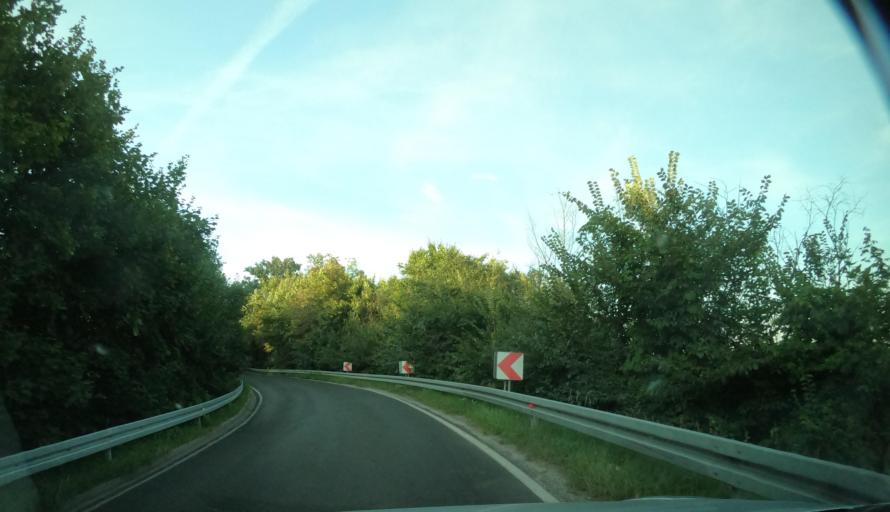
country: PL
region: Kujawsko-Pomorskie
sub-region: Powiat swiecki
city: Pruszcz
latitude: 53.2353
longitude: 18.2186
